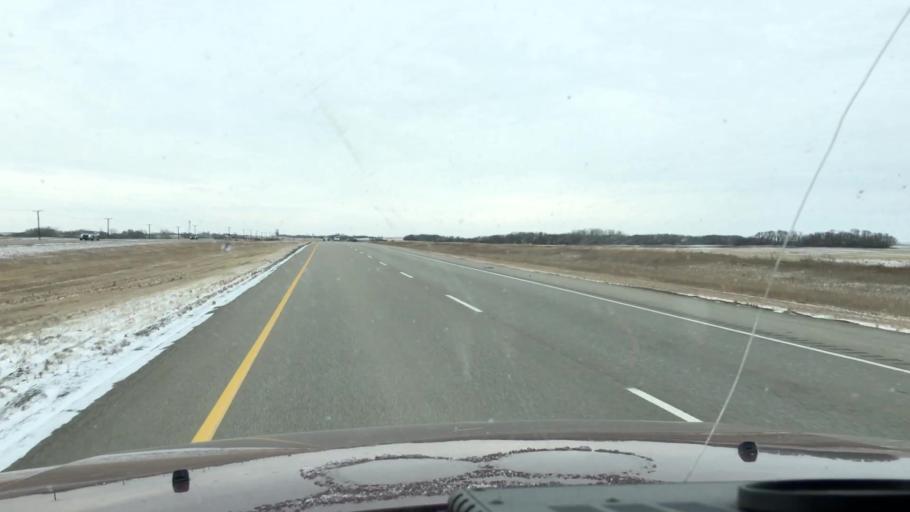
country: CA
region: Saskatchewan
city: Watrous
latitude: 51.3925
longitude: -106.1696
